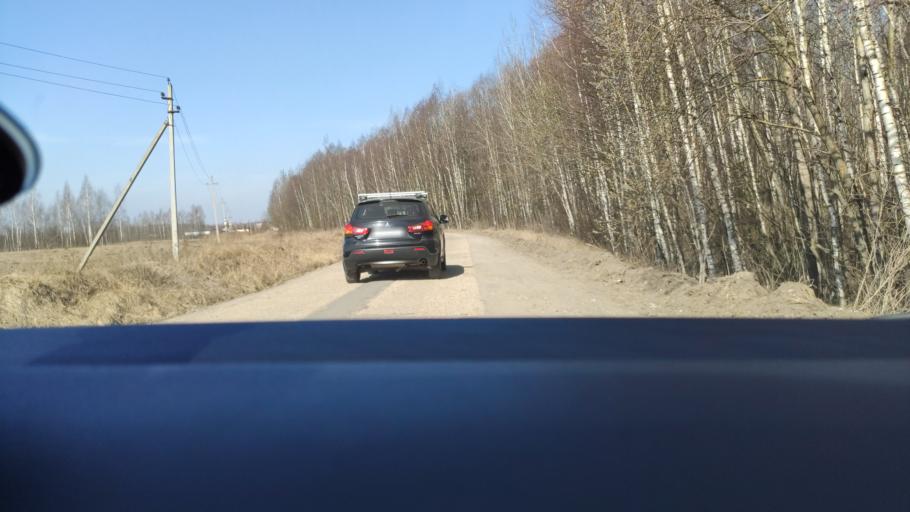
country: RU
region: Moskovskaya
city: Elektrostal'
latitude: 55.7739
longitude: 38.3800
